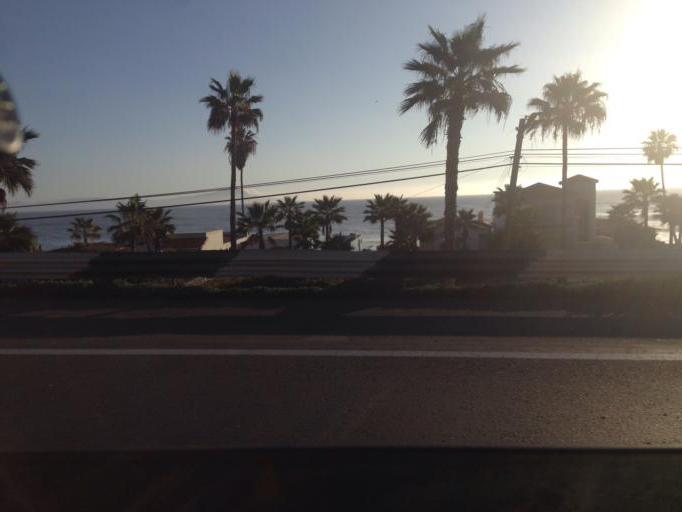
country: MX
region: Baja California
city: El Sauzal
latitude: 31.8672
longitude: -116.6719
